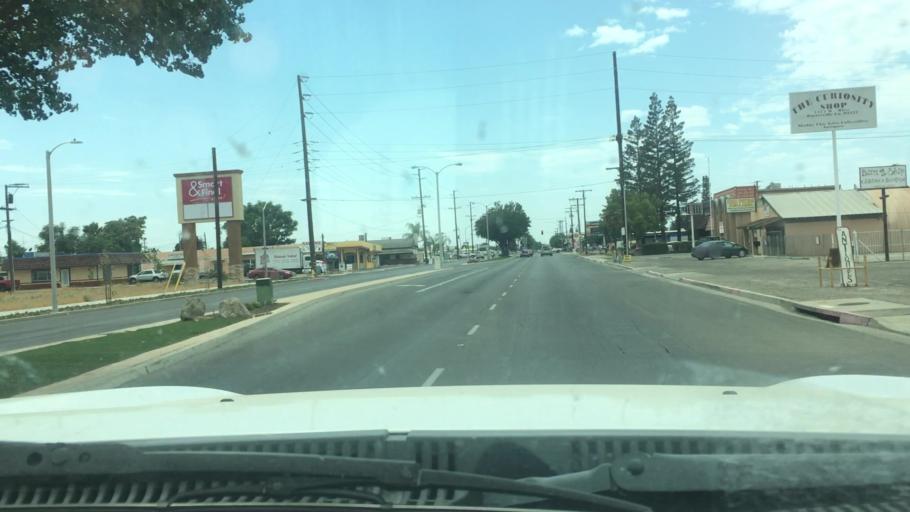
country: US
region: California
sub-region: Tulare County
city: Porterville
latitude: 36.0659
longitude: -119.0499
